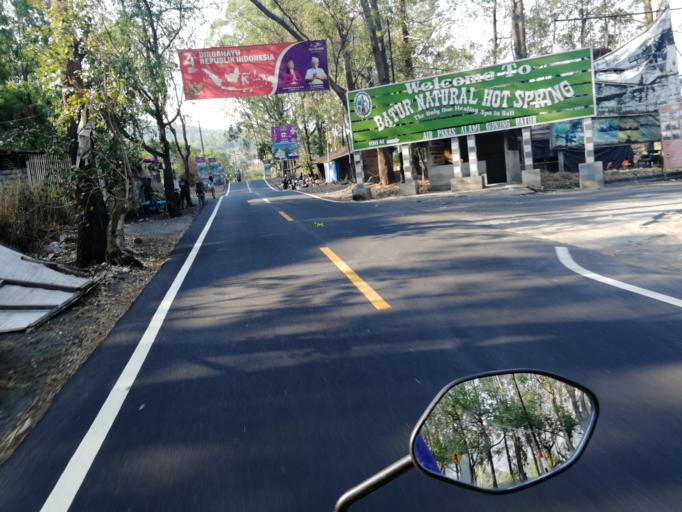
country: ID
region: Bali
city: Banjar Trunyan
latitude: -8.2523
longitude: 115.3968
